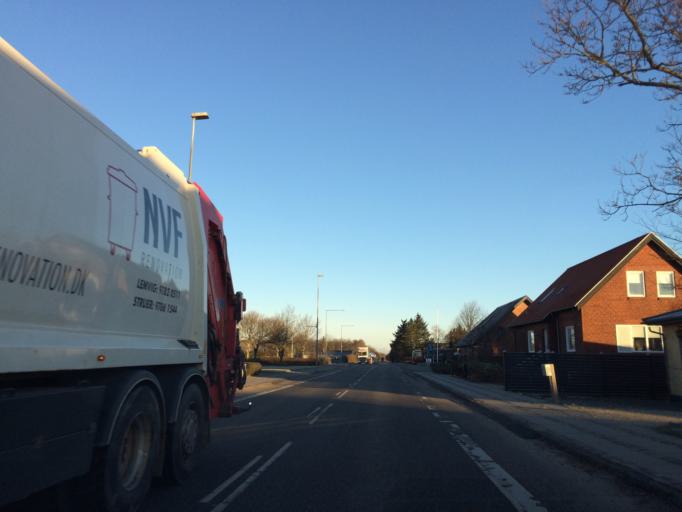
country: DK
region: Central Jutland
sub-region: Holstebro Kommune
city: Ulfborg
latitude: 56.3460
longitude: 8.3424
